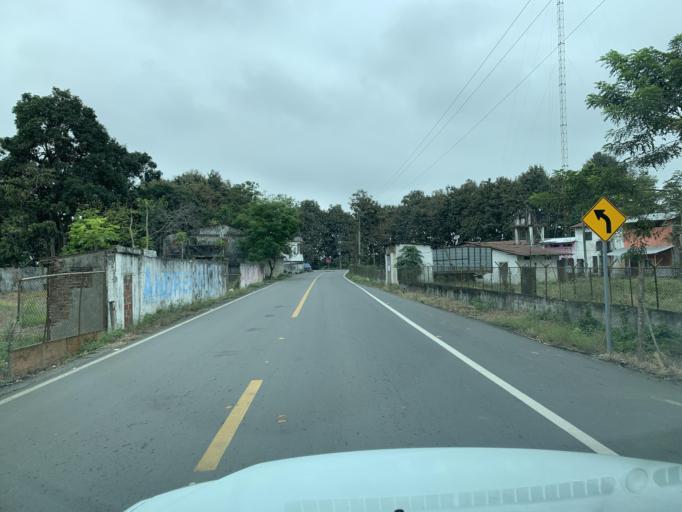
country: EC
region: Guayas
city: Coronel Marcelino Mariduena
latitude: -2.2949
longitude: -79.5028
